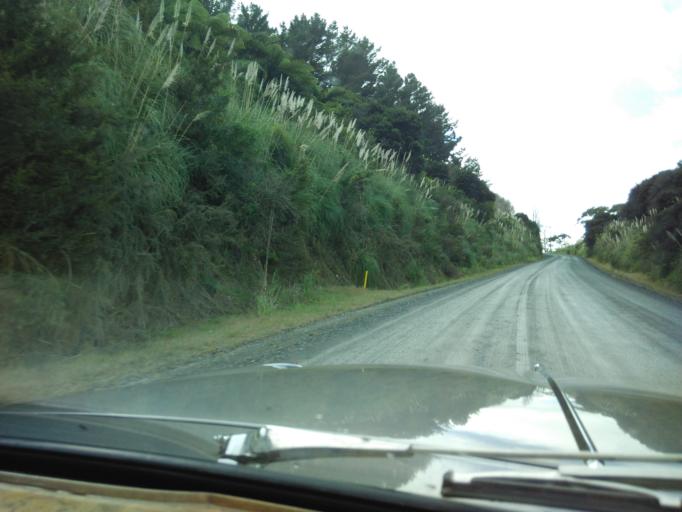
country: NZ
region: Auckland
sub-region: Auckland
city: Wellsford
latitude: -36.3483
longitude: 174.3484
